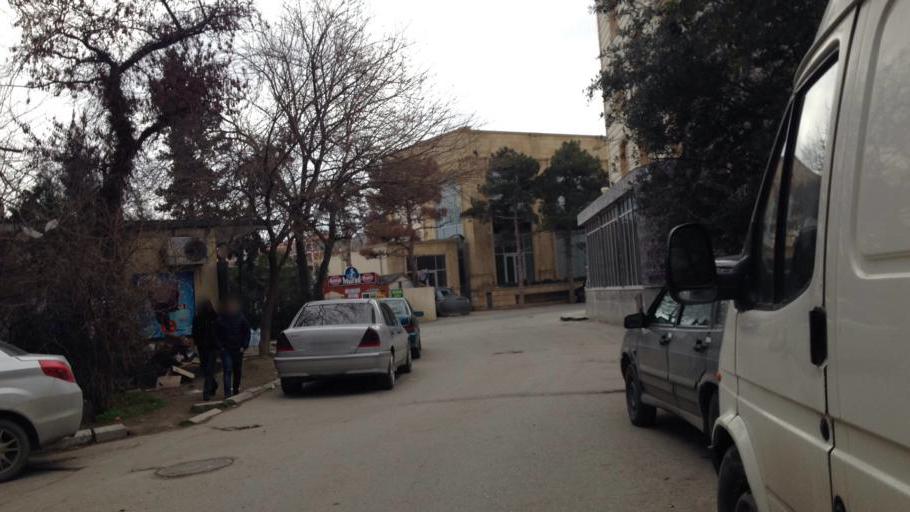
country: AZ
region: Baki
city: Bilajari
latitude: 40.4083
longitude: 49.8364
